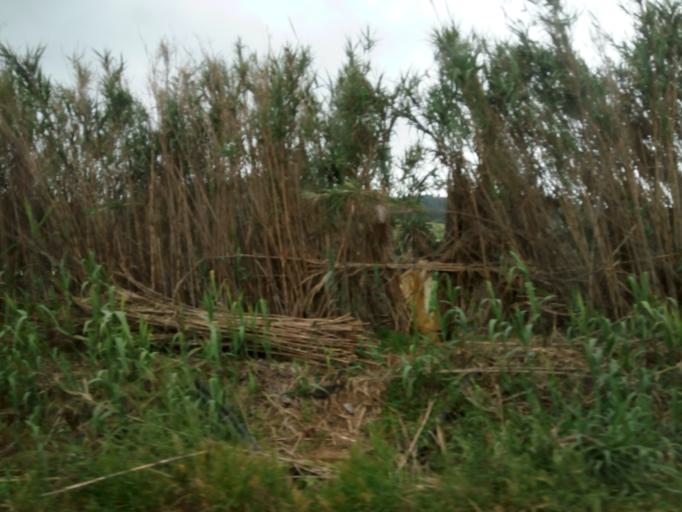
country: DZ
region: Tipaza
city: Tipasa
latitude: 36.5898
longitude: 2.5236
